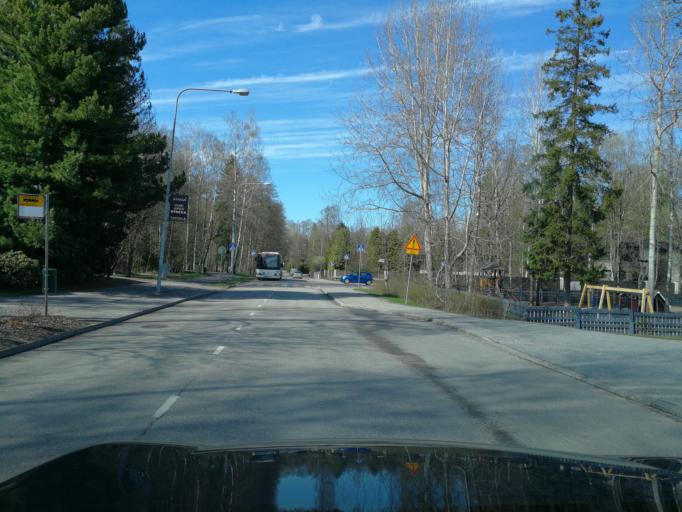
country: FI
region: Uusimaa
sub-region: Helsinki
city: Koukkuniemi
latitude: 60.1632
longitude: 24.7906
